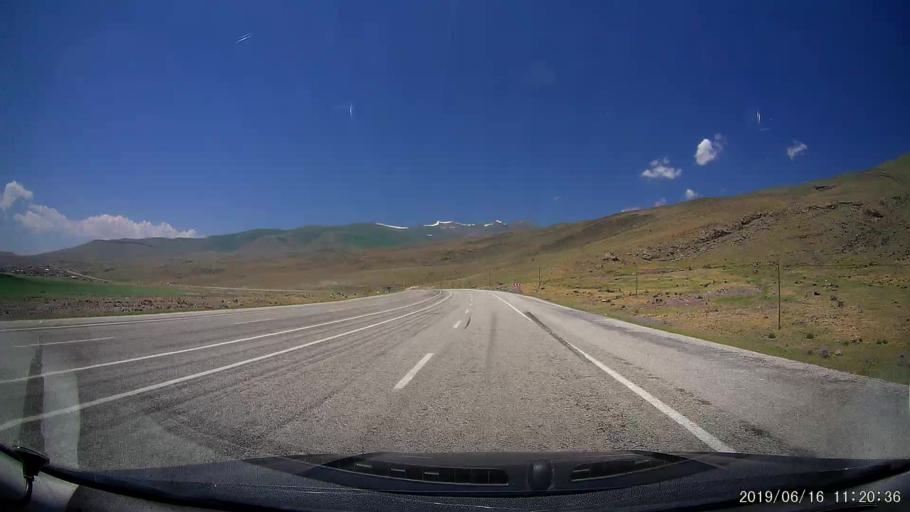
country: TR
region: Agri
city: Dogubayazit
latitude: 39.6995
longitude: 44.0881
